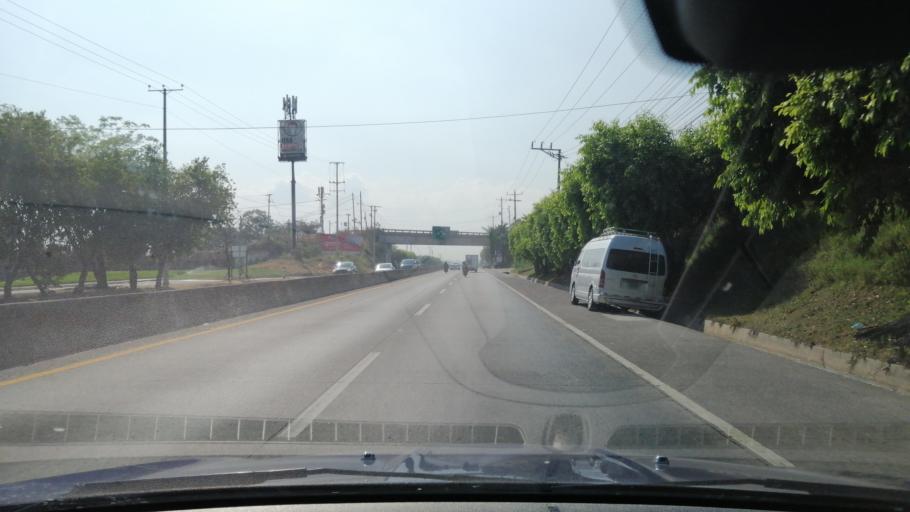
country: SV
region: San Salvador
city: Apopa
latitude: 13.7982
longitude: -89.2300
